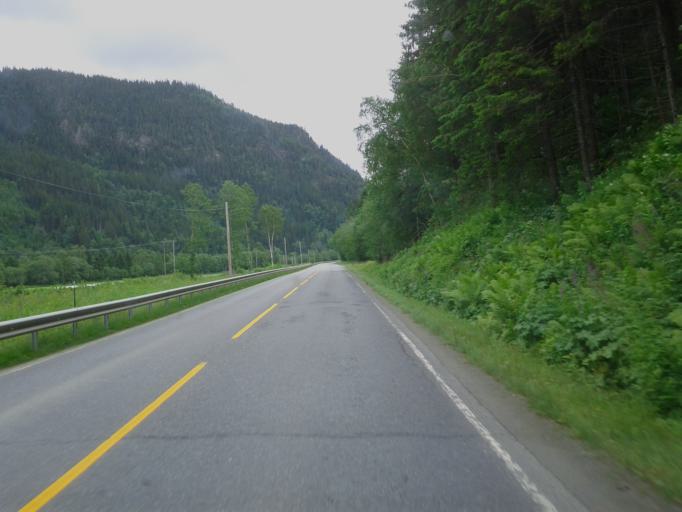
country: NO
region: Sor-Trondelag
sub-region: Midtre Gauldal
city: Storen
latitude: 62.9911
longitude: 10.5272
